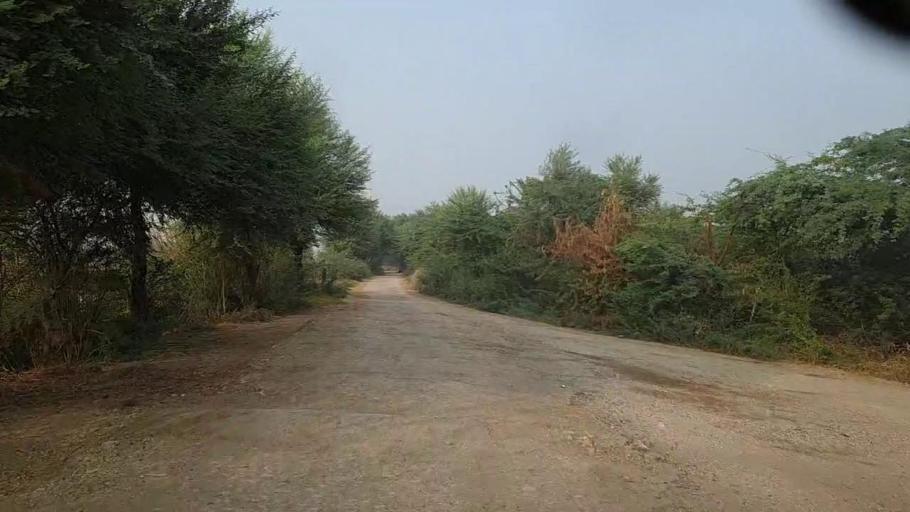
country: PK
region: Sindh
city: Bozdar
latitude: 27.1573
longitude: 68.6605
